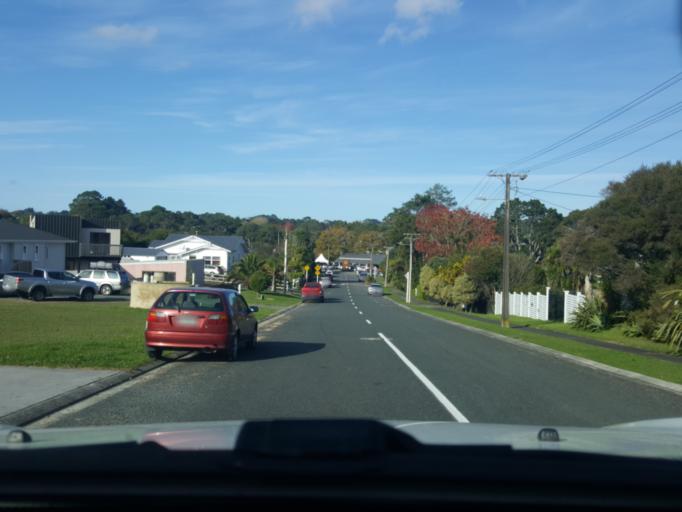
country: NZ
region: Auckland
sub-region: Auckland
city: Rosebank
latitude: -36.7587
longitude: 174.5953
